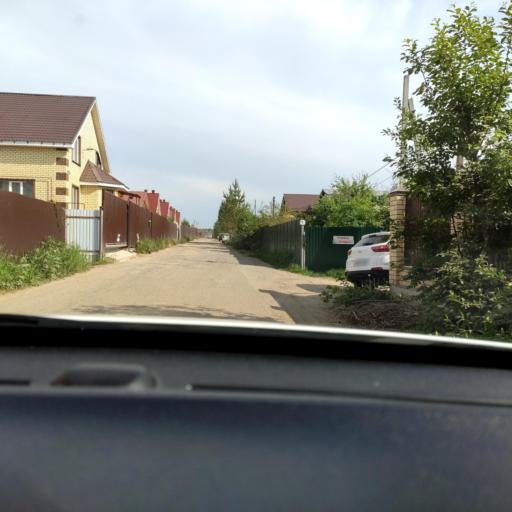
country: RU
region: Tatarstan
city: Vysokaya Gora
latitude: 55.8160
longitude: 49.2874
